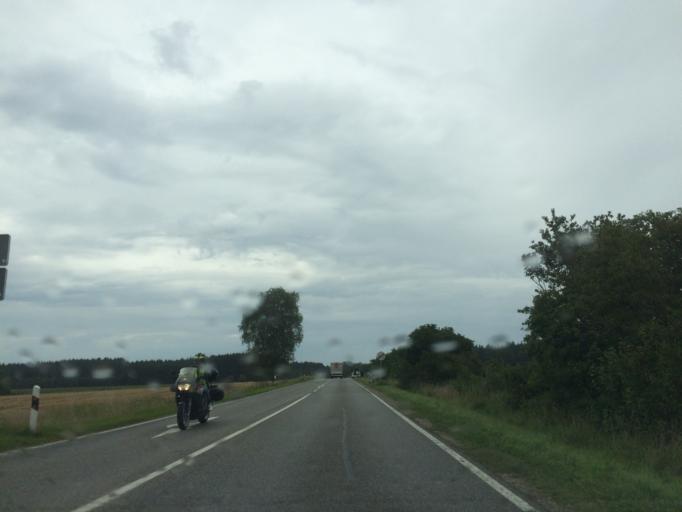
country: DE
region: Baden-Wuerttemberg
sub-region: Tuebingen Region
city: Eberhardzell
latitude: 47.9653
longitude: 9.8104
